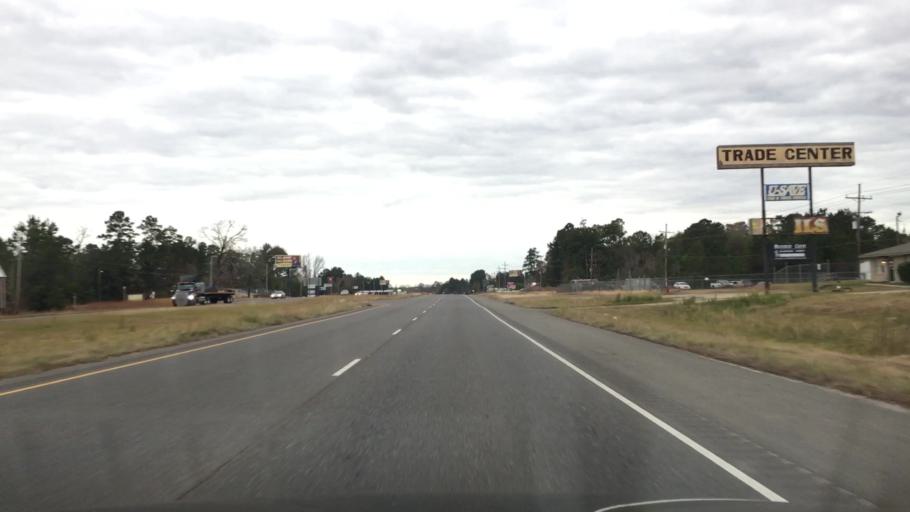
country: US
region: Louisiana
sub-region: Vernon Parish
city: New Llano
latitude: 31.0798
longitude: -93.2727
